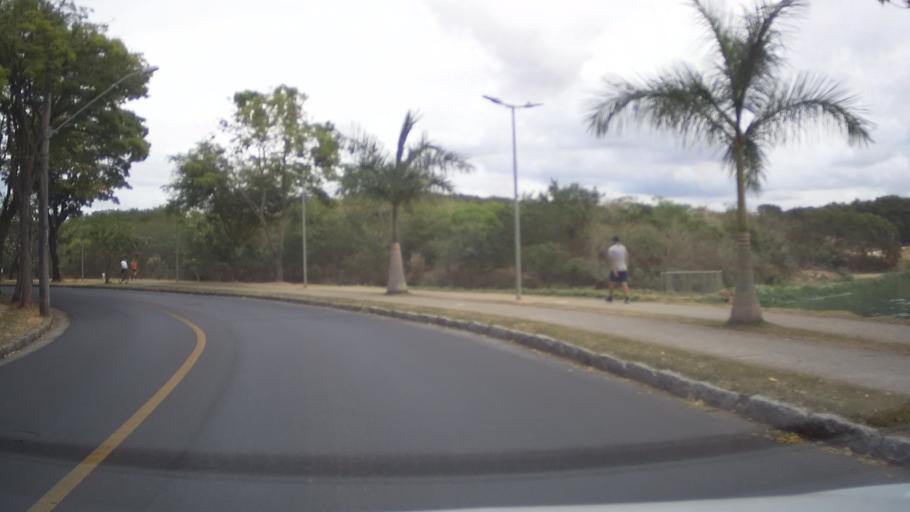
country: BR
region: Minas Gerais
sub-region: Belo Horizonte
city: Belo Horizonte
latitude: -19.8498
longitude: -43.9917
